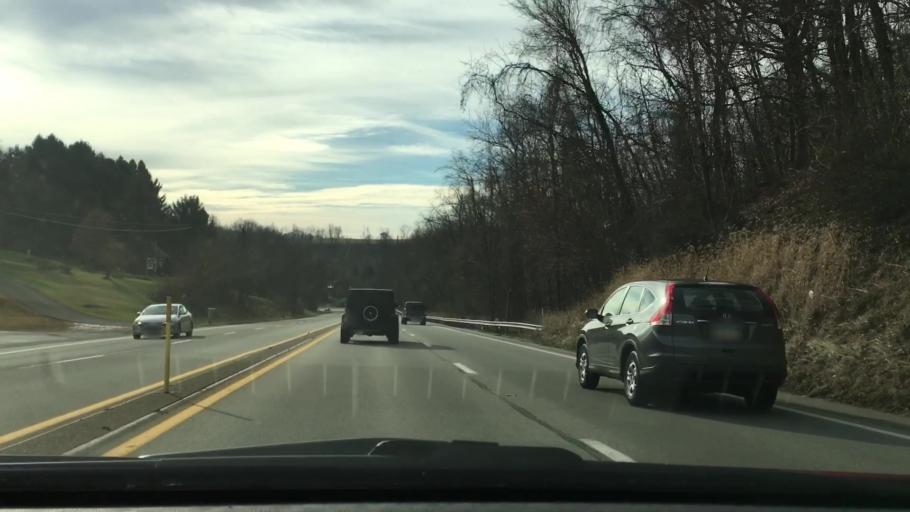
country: US
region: Pennsylvania
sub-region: Fayette County
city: Perryopolis
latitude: 40.0171
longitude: -79.7657
